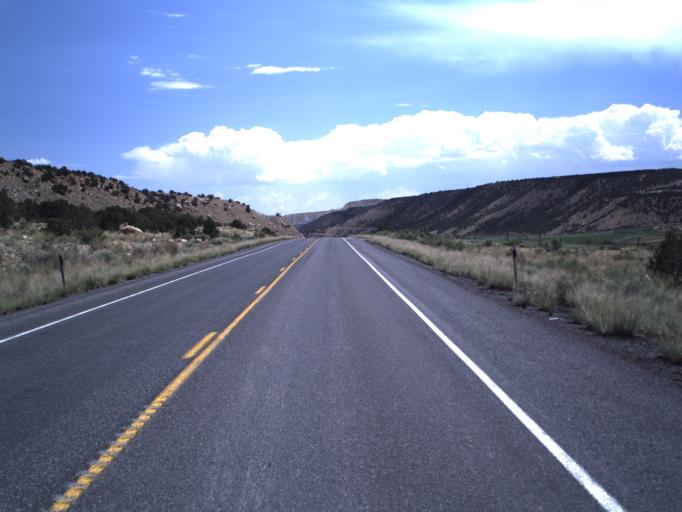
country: US
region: Utah
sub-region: Emery County
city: Huntington
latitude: 39.3833
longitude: -111.0751
